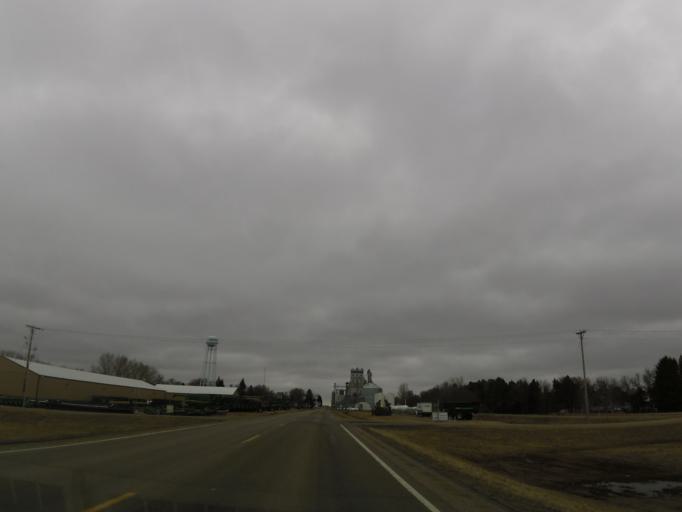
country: US
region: North Dakota
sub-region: Traill County
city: Hillsboro
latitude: 47.1957
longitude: -97.2175
